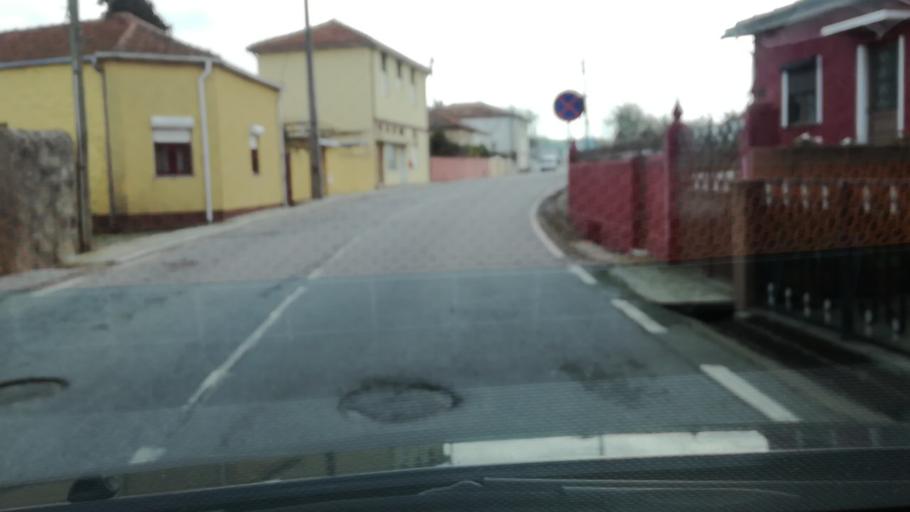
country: PT
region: Porto
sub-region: Maia
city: Gemunde
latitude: 41.2649
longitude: -8.6484
